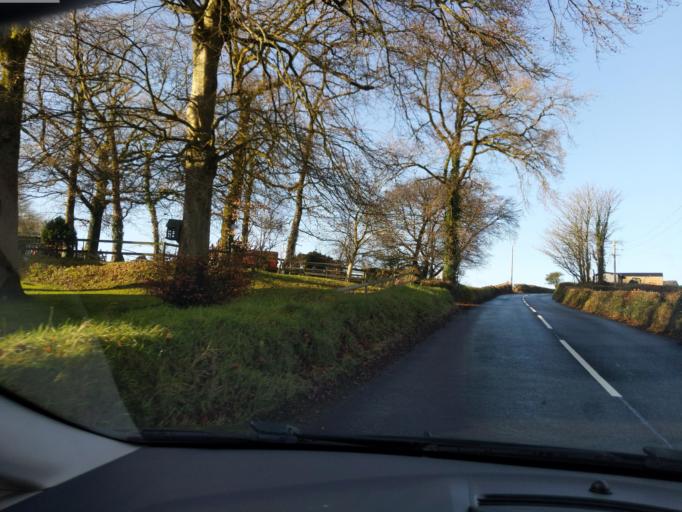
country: GB
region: England
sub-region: Devon
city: Okehampton
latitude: 50.7484
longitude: -4.0233
